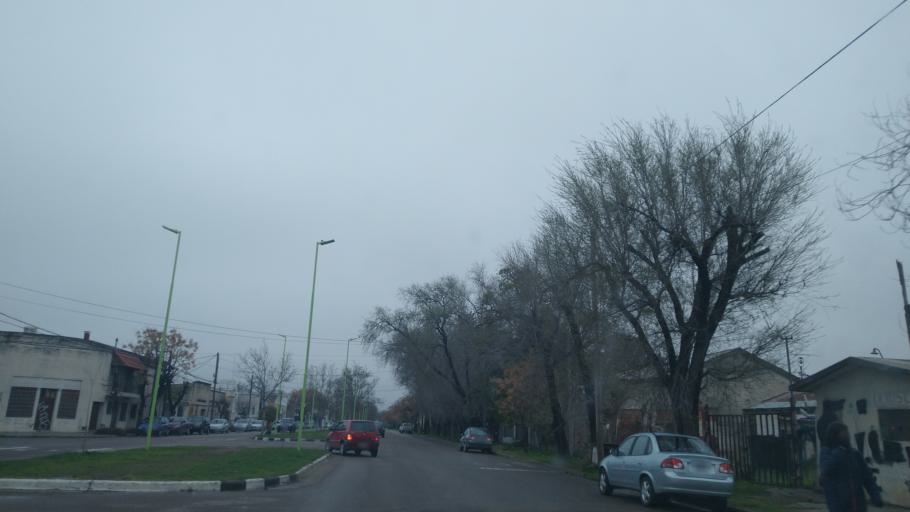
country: AR
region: Buenos Aires
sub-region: Partido de Bahia Blanca
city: Bahia Blanca
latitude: -38.7311
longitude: -62.2520
